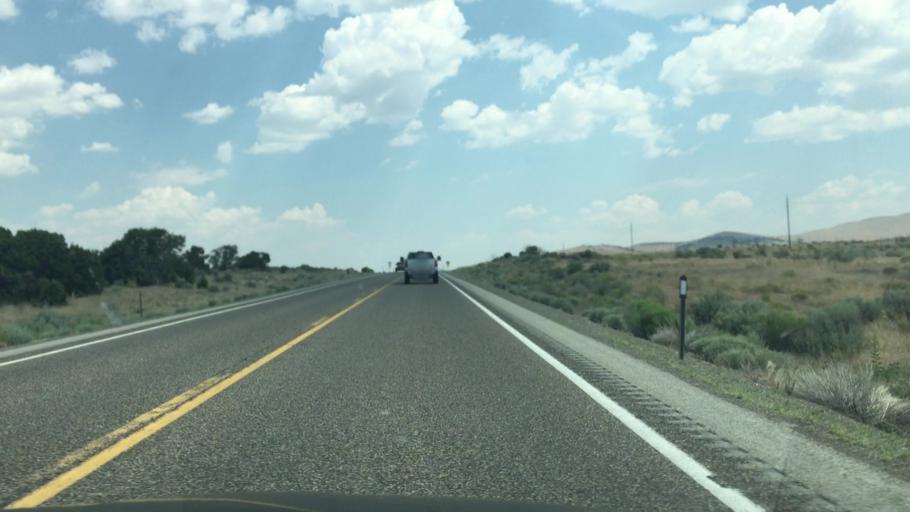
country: US
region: Nevada
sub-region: Elko County
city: Wells
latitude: 41.2025
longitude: -114.8573
